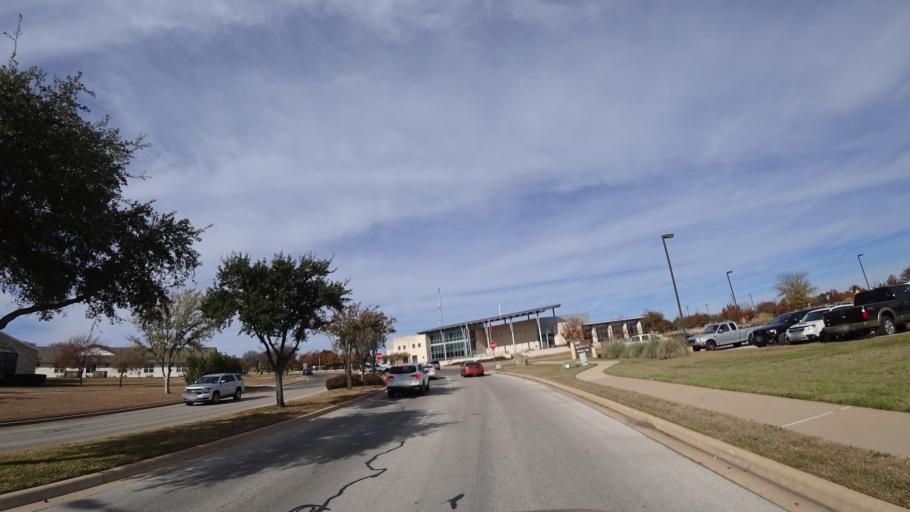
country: US
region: Texas
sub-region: Williamson County
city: Cedar Park
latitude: 30.5194
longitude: -97.8236
